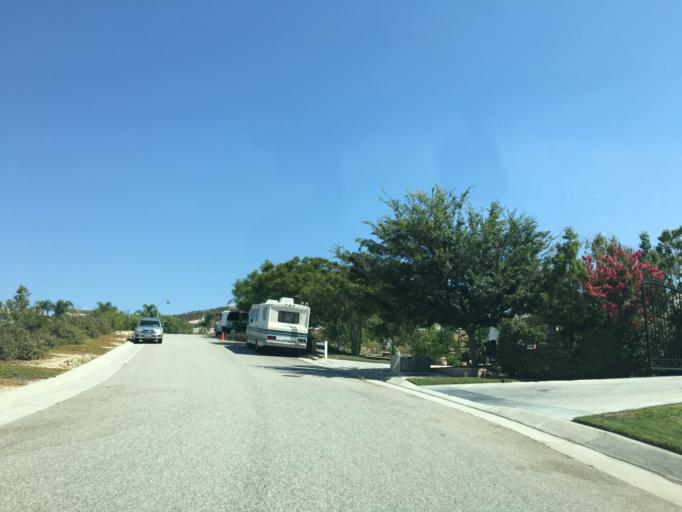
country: US
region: California
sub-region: Los Angeles County
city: Val Verde
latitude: 34.4713
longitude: -118.6473
